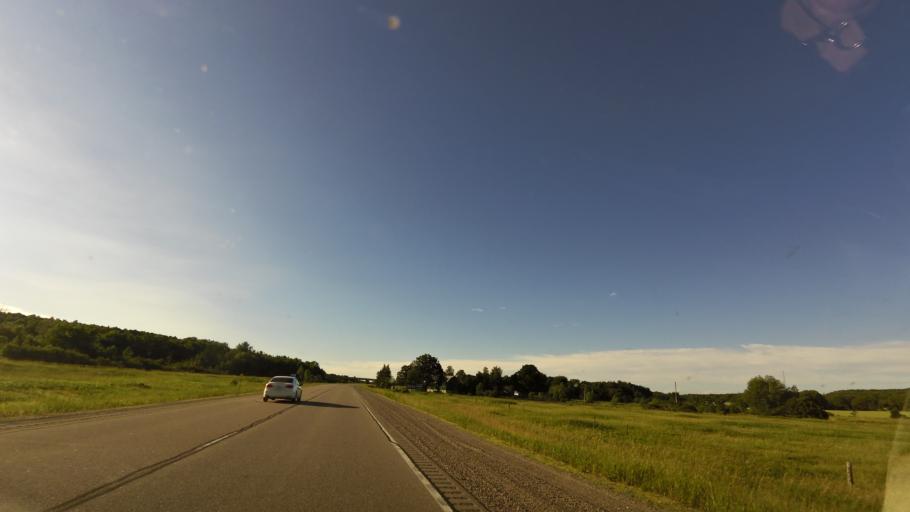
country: CA
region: Ontario
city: Orillia
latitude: 44.6790
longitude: -79.6457
